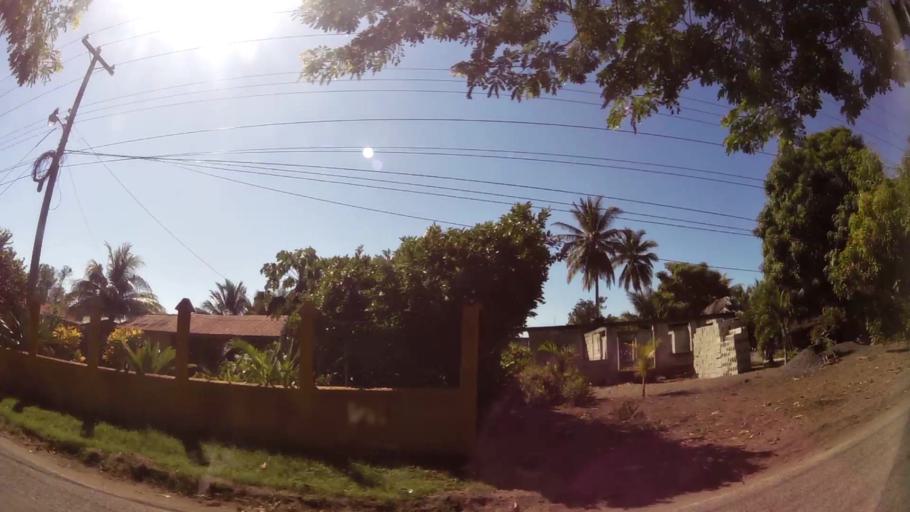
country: GT
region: Escuintla
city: Iztapa
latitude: 13.9245
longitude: -90.5831
